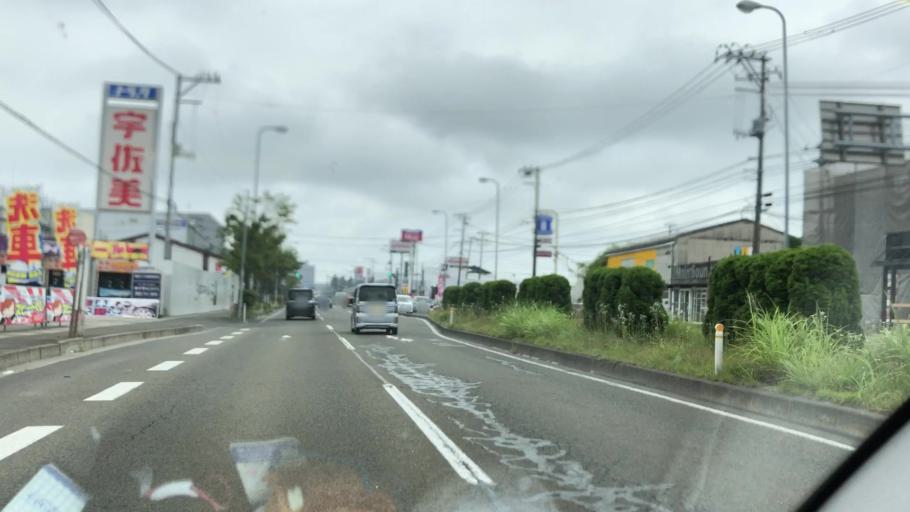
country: JP
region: Miyagi
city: Rifu
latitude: 38.2698
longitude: 140.9488
